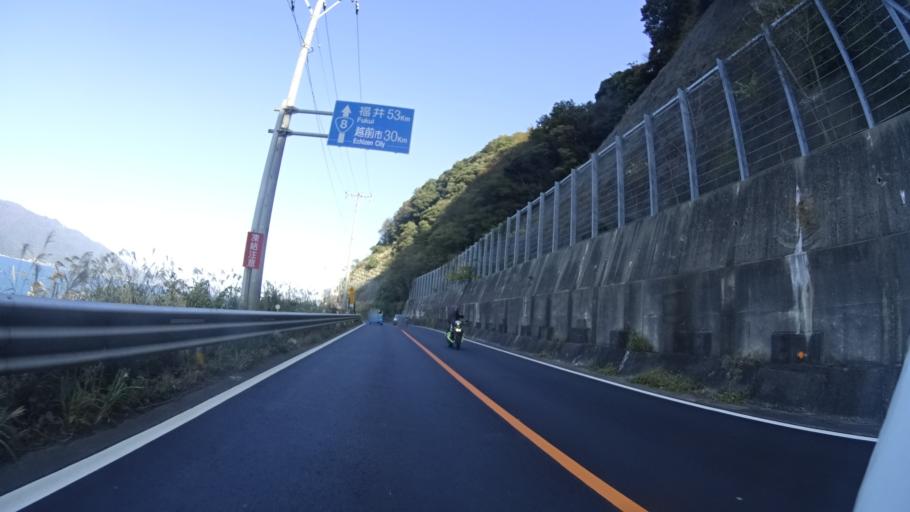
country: JP
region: Fukui
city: Tsuruga
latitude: 35.6941
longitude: 136.0815
